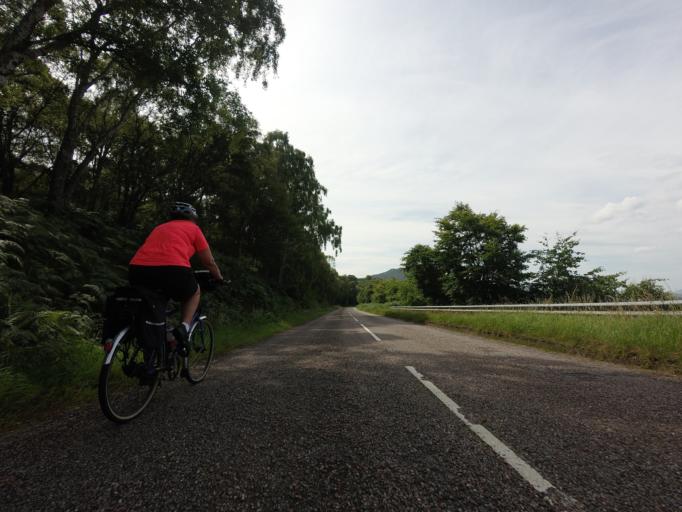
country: GB
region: Scotland
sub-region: Highland
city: Alness
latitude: 57.8508
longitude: -4.2652
